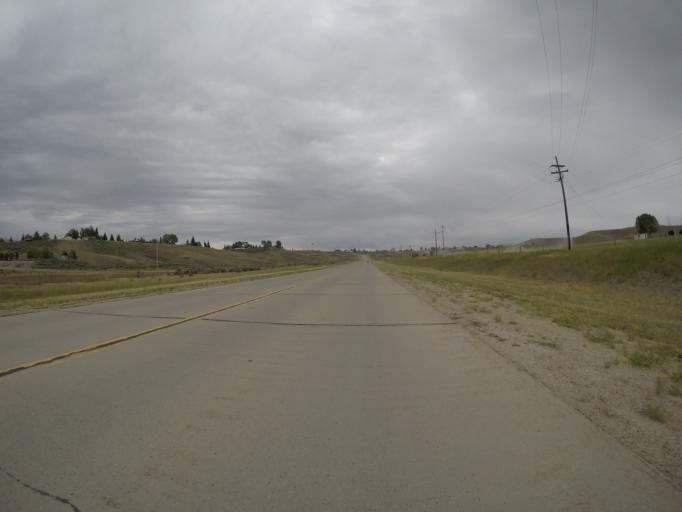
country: US
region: Wyoming
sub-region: Lincoln County
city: Kemmerer
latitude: 41.7994
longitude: -110.5477
